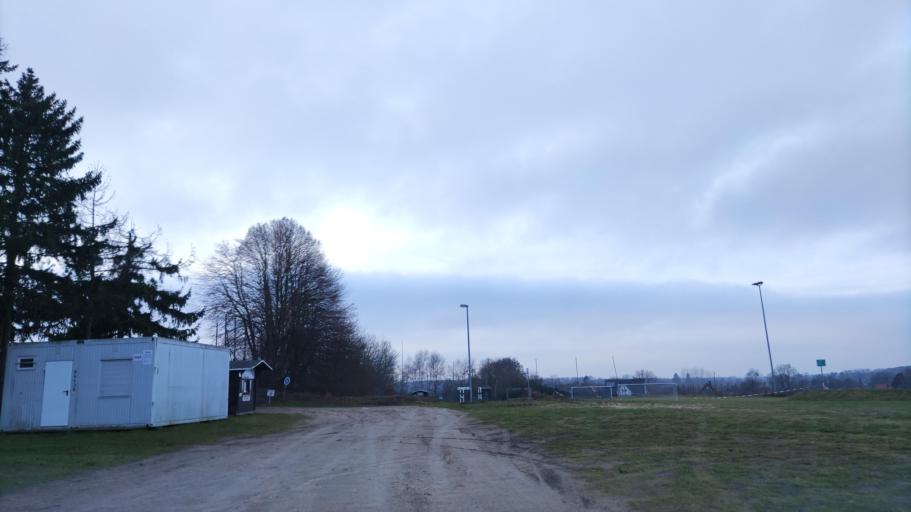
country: DE
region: Lower Saxony
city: Neetze
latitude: 53.2683
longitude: 10.6322
